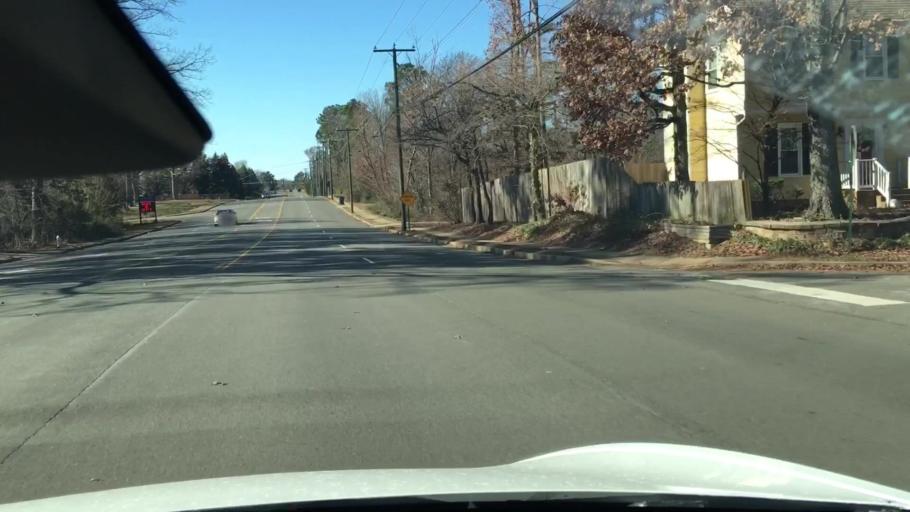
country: US
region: Virginia
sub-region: Henrico County
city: Laurel
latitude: 37.6494
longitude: -77.5435
